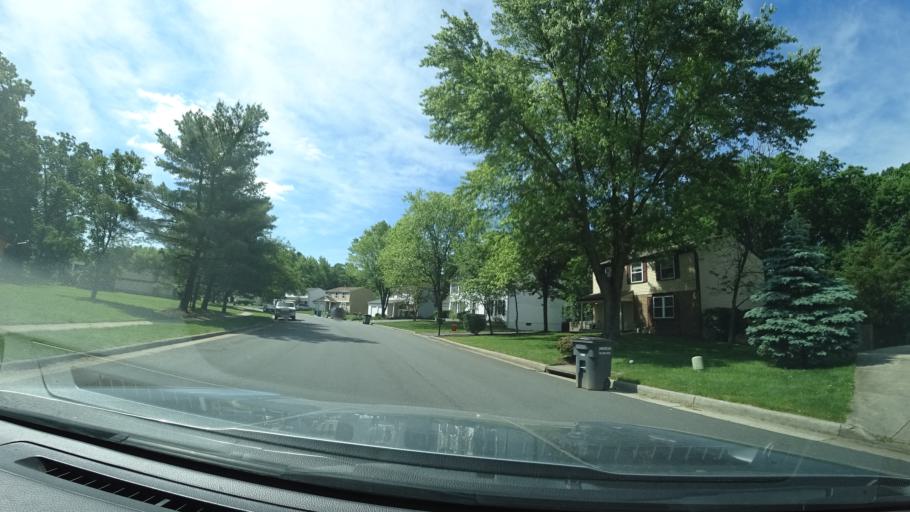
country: US
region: Virginia
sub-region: Loudoun County
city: Oak Grove
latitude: 38.9886
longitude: -77.4067
